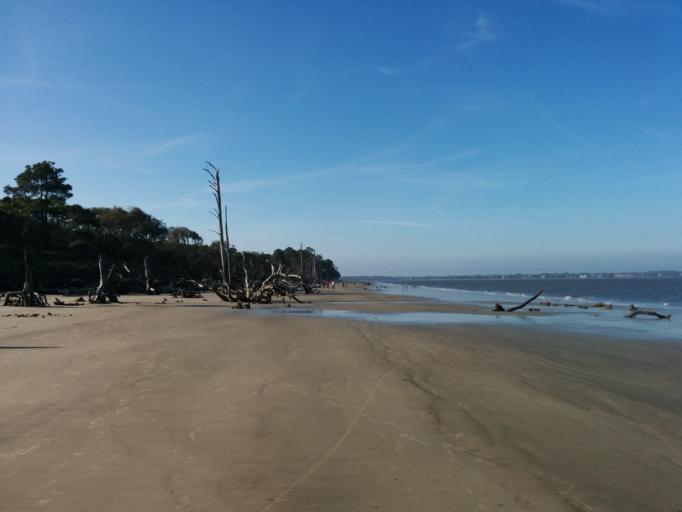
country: US
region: Georgia
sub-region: Glynn County
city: Saint Simons Island
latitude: 31.1073
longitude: -81.4049
